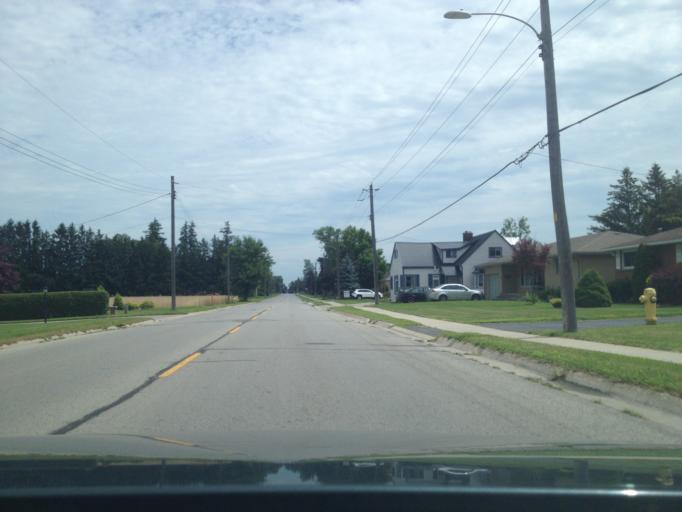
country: CA
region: Ontario
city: Norfolk County
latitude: 42.8549
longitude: -80.4865
